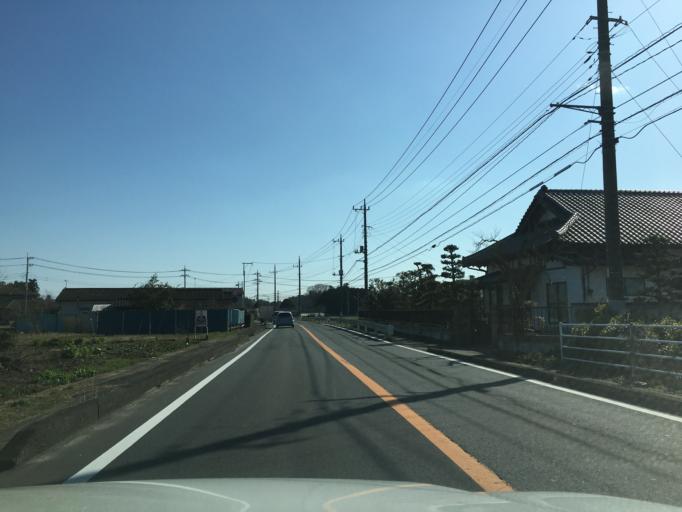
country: JP
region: Ibaraki
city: Omiya
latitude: 36.4997
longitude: 140.3718
